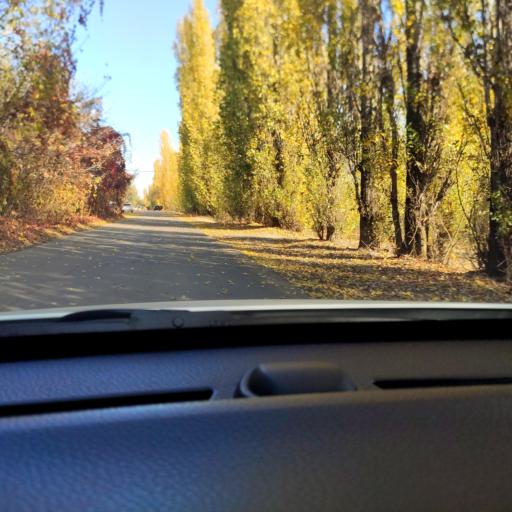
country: RU
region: Voronezj
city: Voronezh
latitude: 51.7048
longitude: 39.2381
